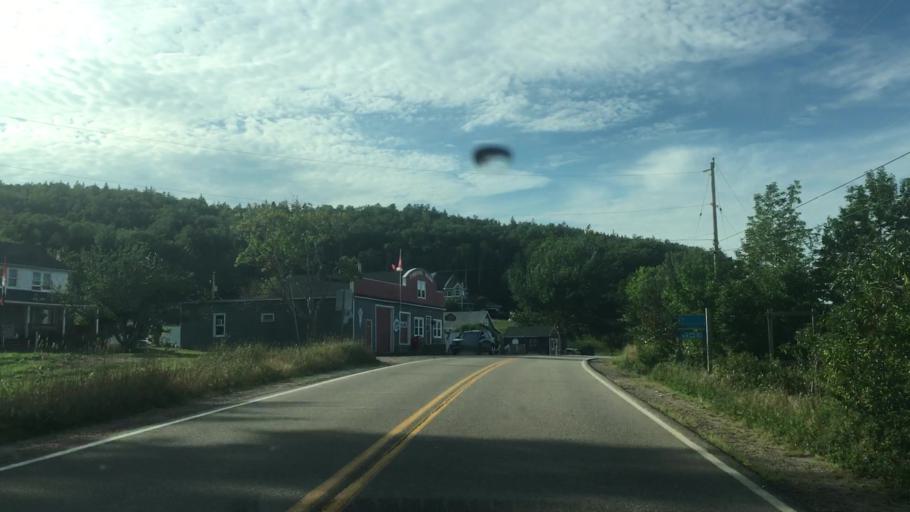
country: CA
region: Nova Scotia
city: Sydney Mines
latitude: 46.8222
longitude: -60.7989
